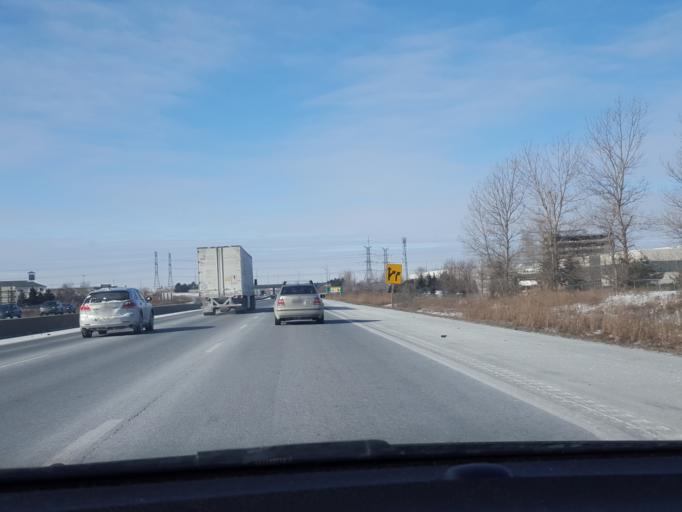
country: CA
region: Ontario
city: Brampton
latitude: 43.6012
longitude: -79.7782
